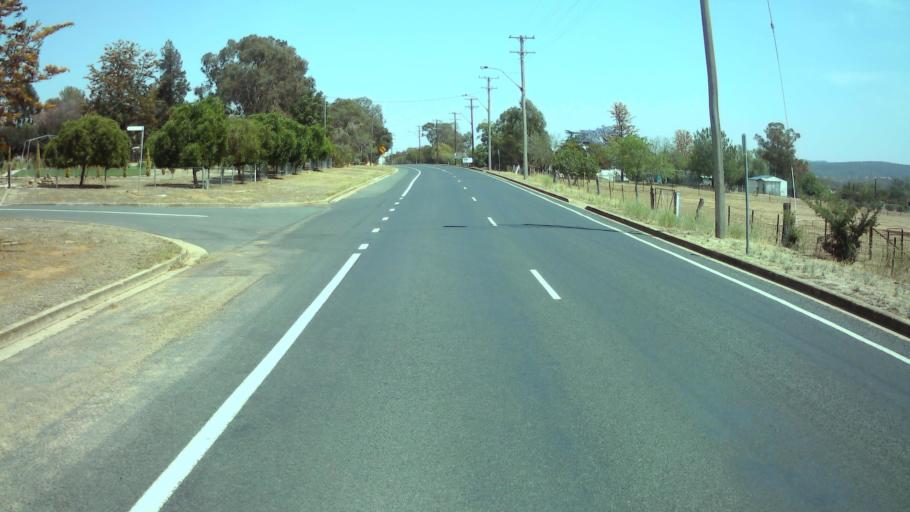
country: AU
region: New South Wales
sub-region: Weddin
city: Grenfell
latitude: -33.8960
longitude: 148.1714
